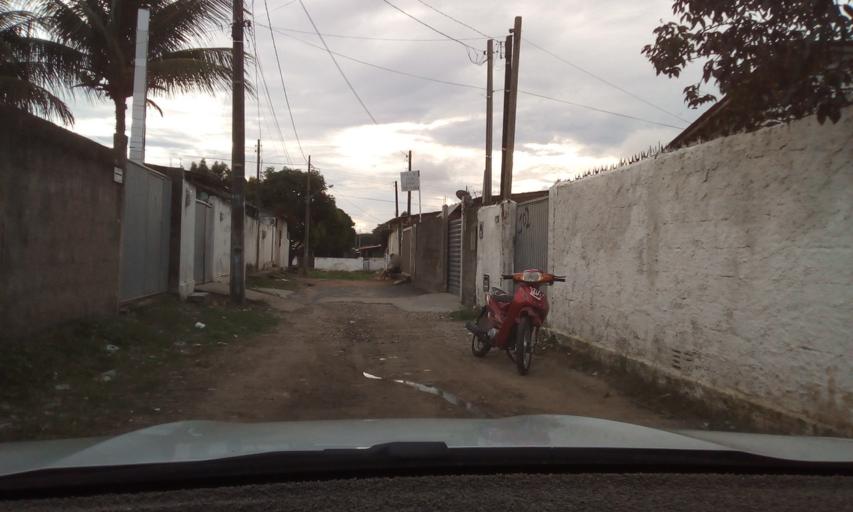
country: BR
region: Paraiba
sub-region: Joao Pessoa
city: Joao Pessoa
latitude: -7.1766
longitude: -34.8202
